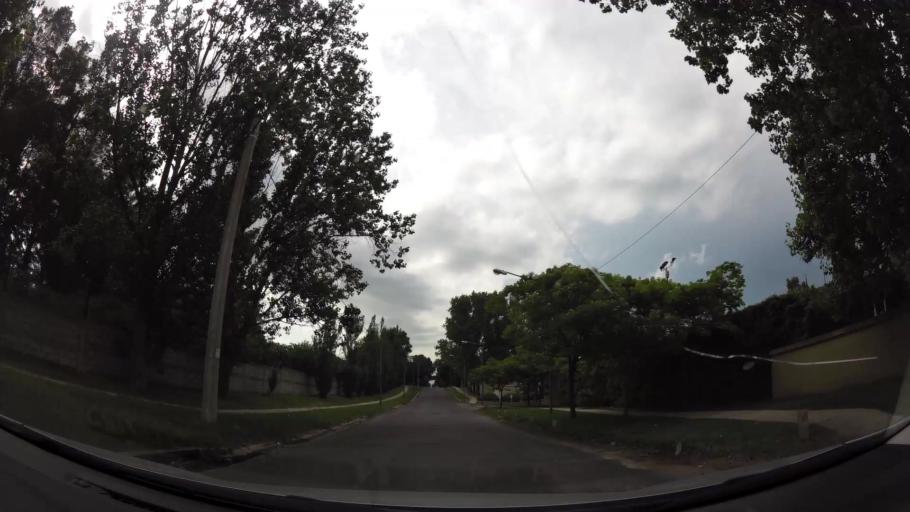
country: AR
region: Buenos Aires
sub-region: Partido de Tigre
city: Tigre
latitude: -34.4791
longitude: -58.6406
